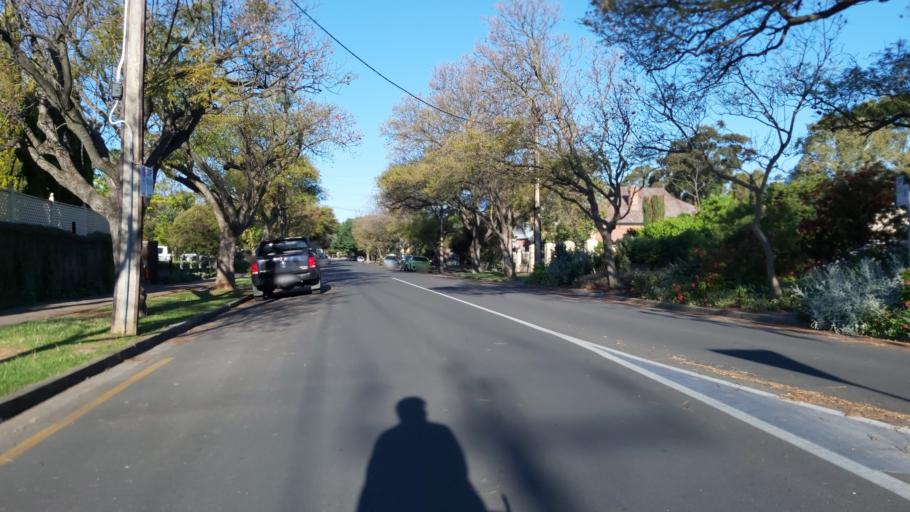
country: AU
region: South Australia
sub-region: Unley
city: Unley
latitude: -34.9453
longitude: 138.5930
